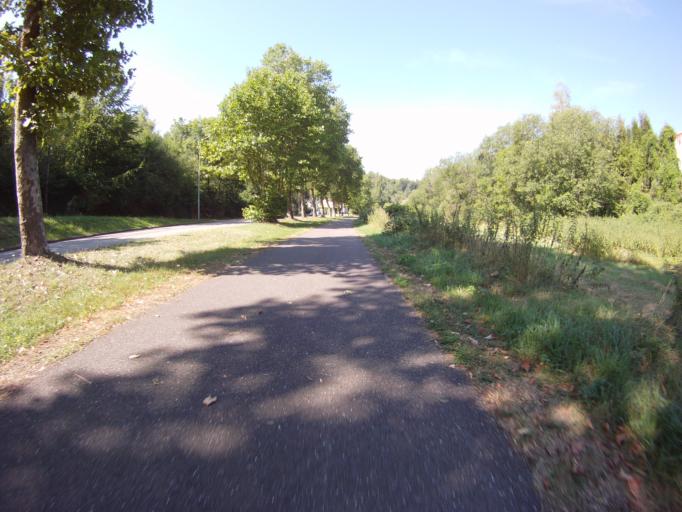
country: FR
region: Lorraine
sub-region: Departement de Meurthe-et-Moselle
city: Liverdun
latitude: 48.7474
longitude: 6.0768
